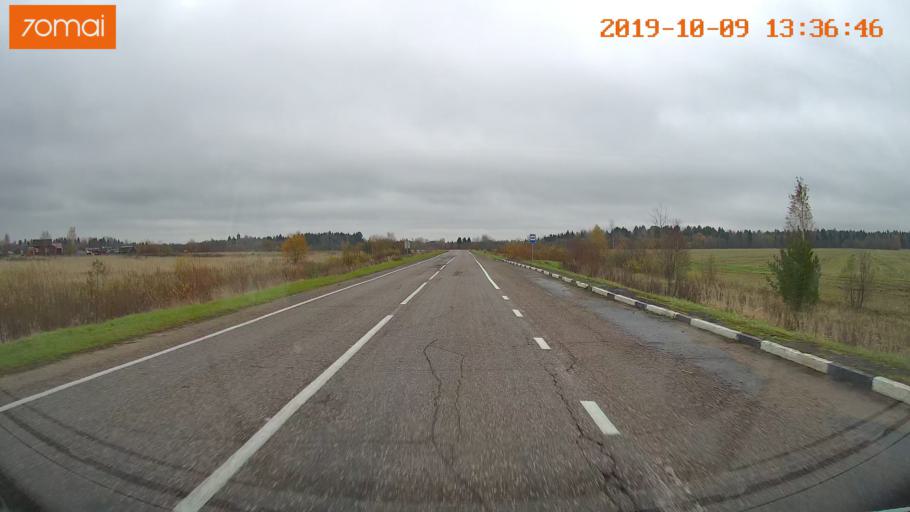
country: RU
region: Jaroslavl
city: Lyubim
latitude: 58.3398
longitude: 41.1039
